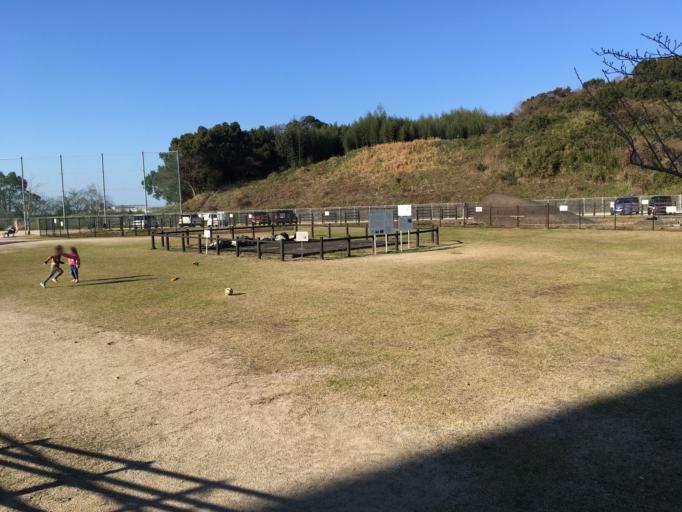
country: JP
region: Fukuoka
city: Umi
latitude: 33.5907
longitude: 130.4865
